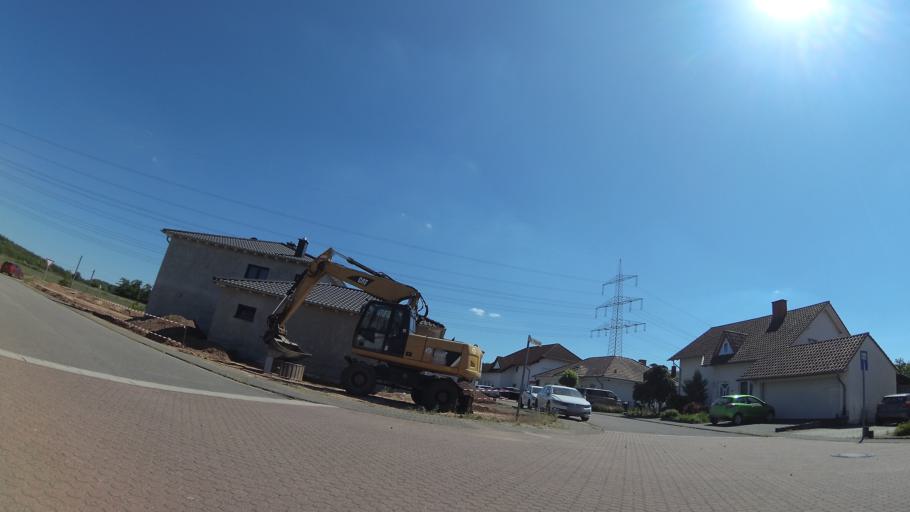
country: DE
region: Saarland
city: Saarwellingen
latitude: 49.3453
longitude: 6.8085
